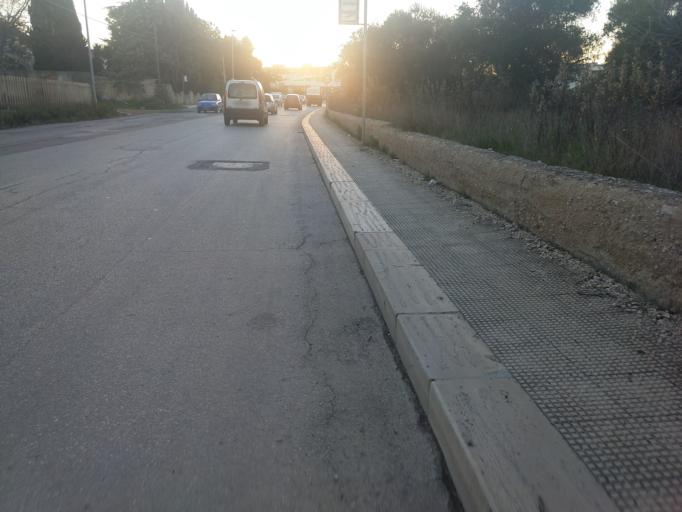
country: IT
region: Apulia
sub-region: Provincia di Bari
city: Modugno
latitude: 41.0830
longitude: 16.7973
